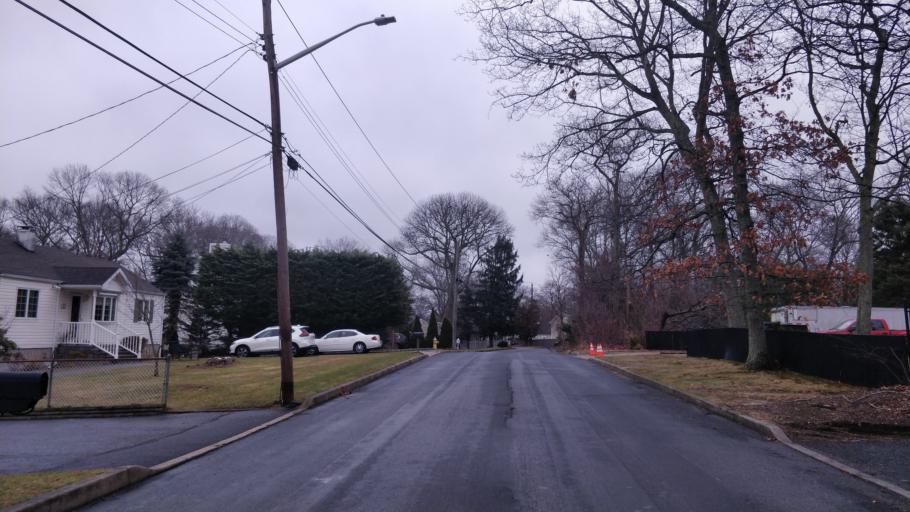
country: US
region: New York
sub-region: Suffolk County
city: Hauppauge
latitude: 40.8312
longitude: -73.2050
